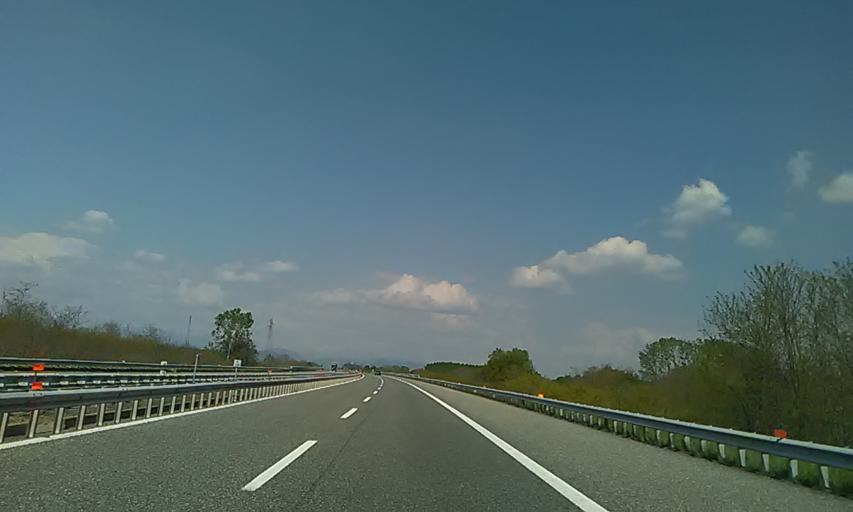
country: IT
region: Piedmont
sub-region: Provincia di Novara
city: Carpignano Sesia
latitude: 45.5357
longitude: 8.4306
